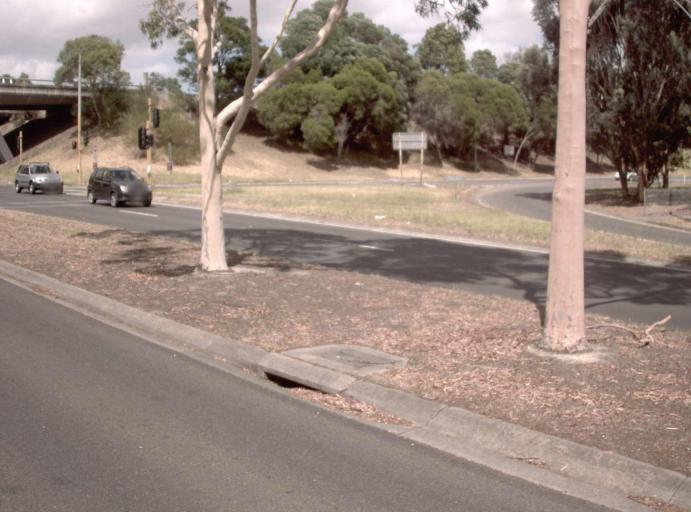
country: AU
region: Victoria
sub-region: Monash
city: Notting Hill
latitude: -37.8920
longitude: 145.1307
